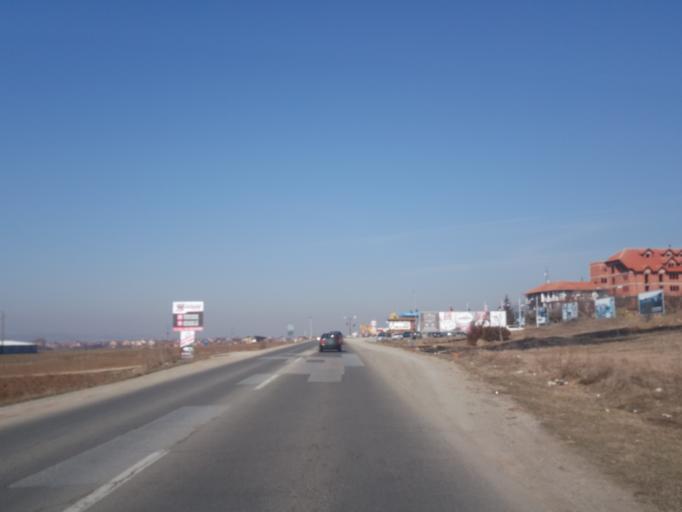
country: XK
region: Mitrovica
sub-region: Vushtrri
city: Vushtrri
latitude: 42.7733
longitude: 21.0181
